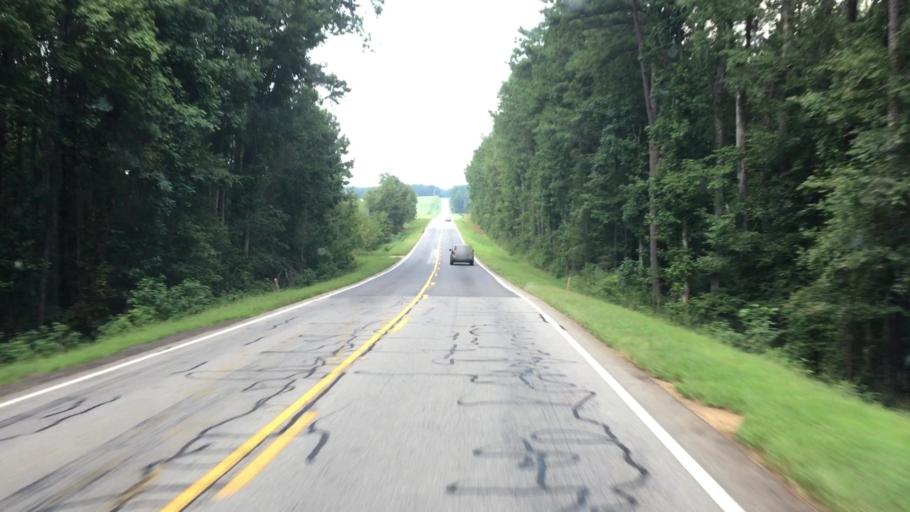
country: US
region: Georgia
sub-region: Jasper County
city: Monticello
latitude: 33.2428
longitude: -83.7225
